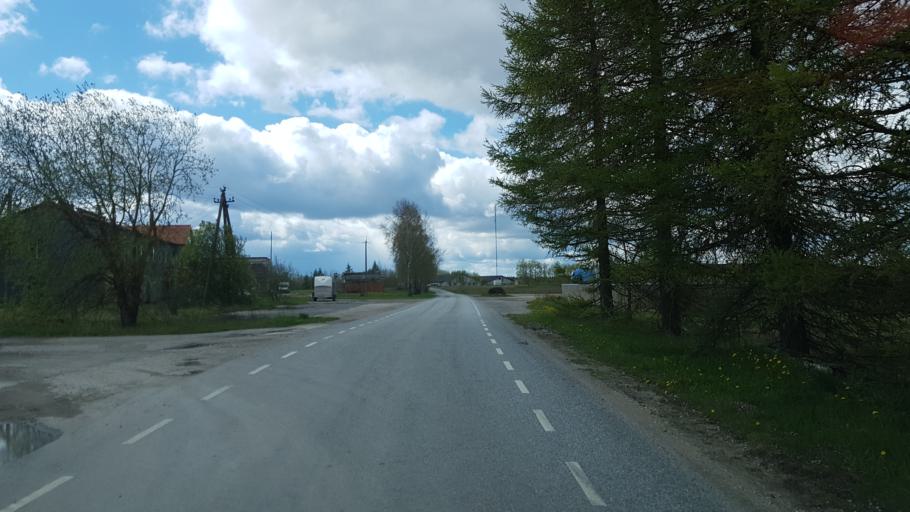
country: EE
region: Raplamaa
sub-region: Kehtna vald
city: Kehtna
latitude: 58.9583
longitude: 24.8391
